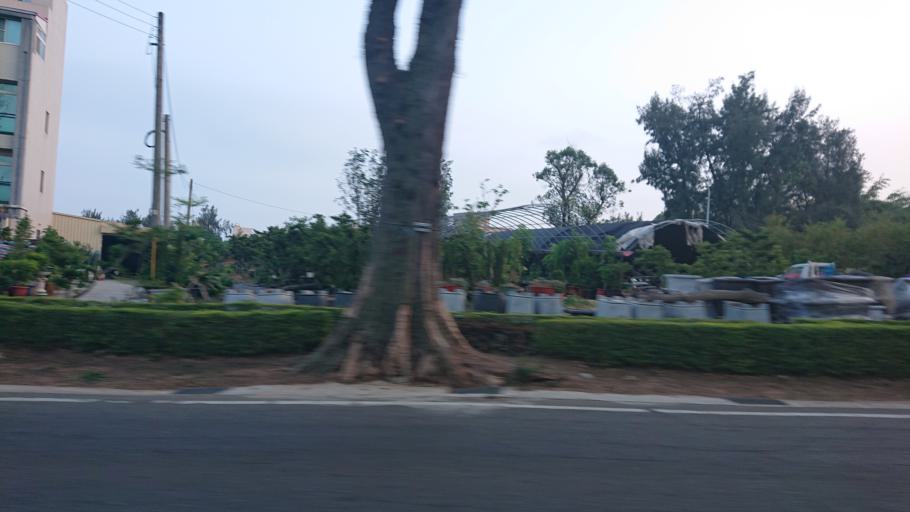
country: TW
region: Fukien
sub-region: Kinmen
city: Jincheng
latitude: 24.4489
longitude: 118.3331
